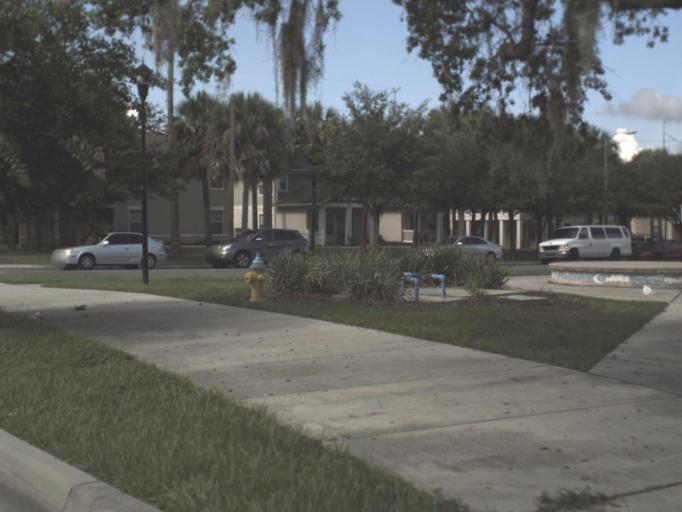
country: US
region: Florida
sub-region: Hillsborough County
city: Tampa
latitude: 27.9790
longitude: -82.4348
